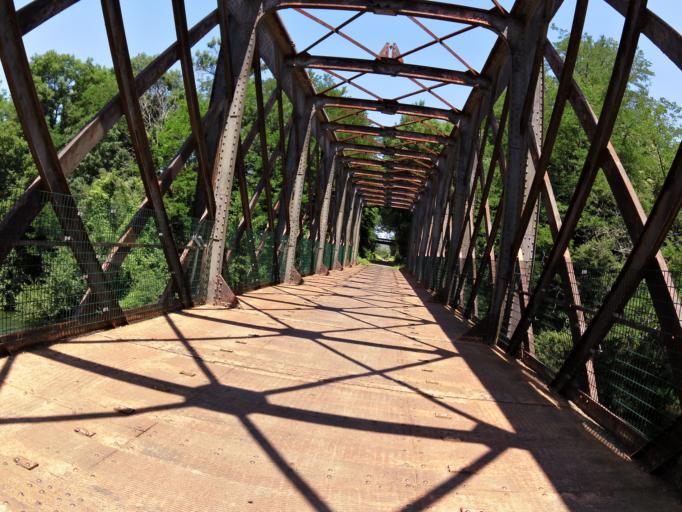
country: FR
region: Aquitaine
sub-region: Departement des Pyrenees-Atlantiques
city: Salies-de-Bearn
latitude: 43.4513
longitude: -0.9938
